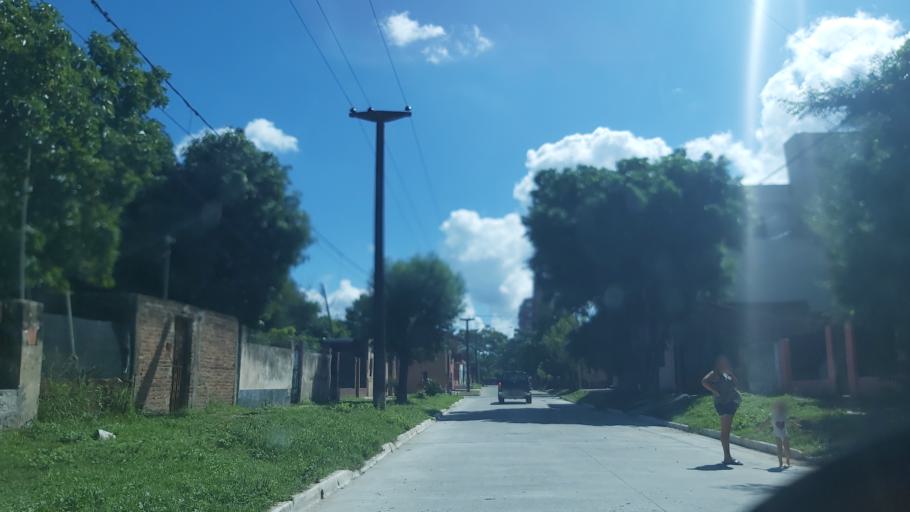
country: AR
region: Corrientes
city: Corrientes
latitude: -27.4772
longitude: -58.8499
